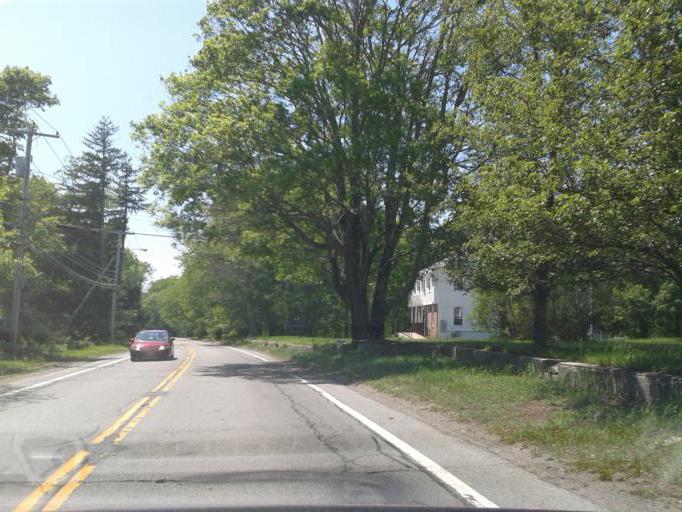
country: US
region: Rhode Island
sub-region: Washington County
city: Kingston
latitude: 41.4827
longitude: -71.5411
